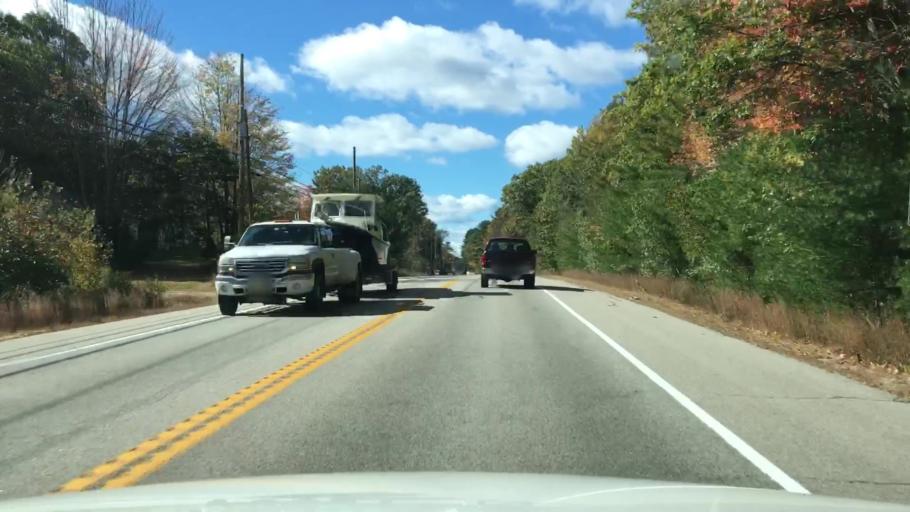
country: US
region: Maine
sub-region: York County
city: Alfred
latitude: 43.4764
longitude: -70.6748
